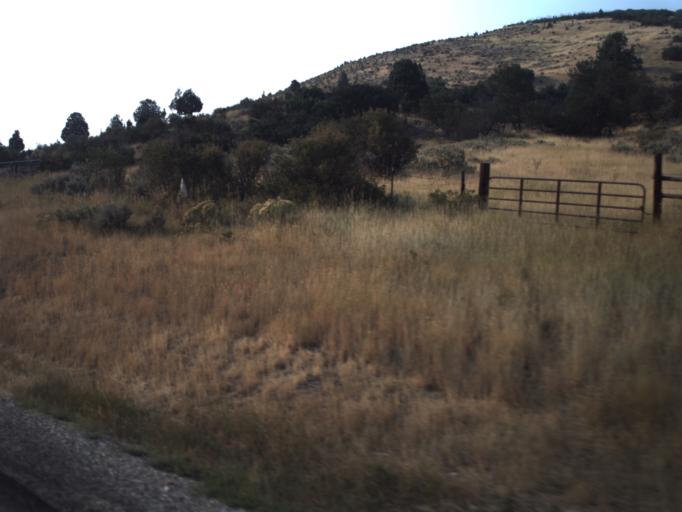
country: US
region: Utah
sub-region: Summit County
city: Kamas
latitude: 40.6310
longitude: -111.2511
